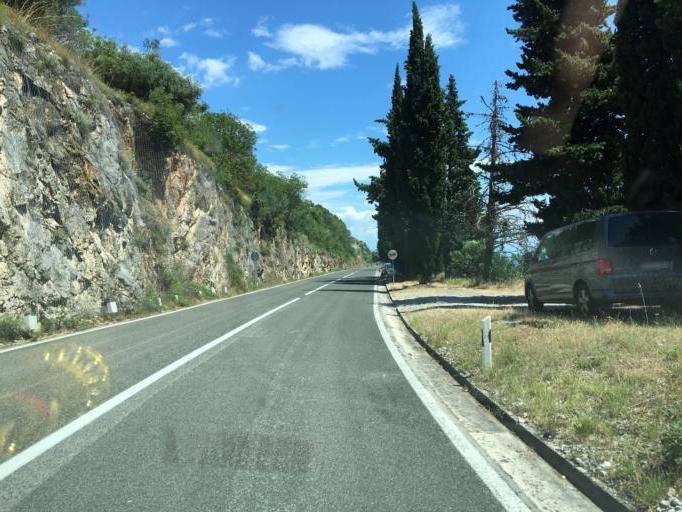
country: HR
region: Istarska
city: Lovran
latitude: 45.2145
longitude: 14.2435
